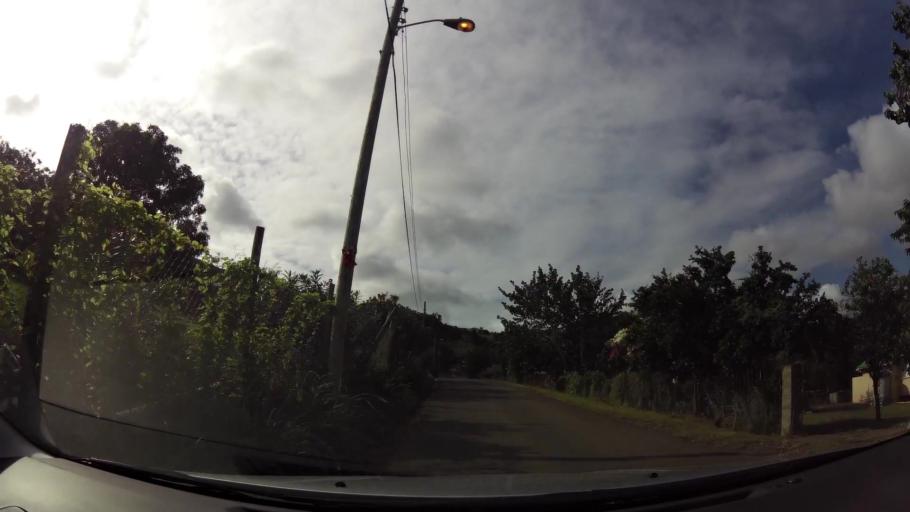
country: AG
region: Saint Paul
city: Falmouth
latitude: 17.0281
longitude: -61.7885
